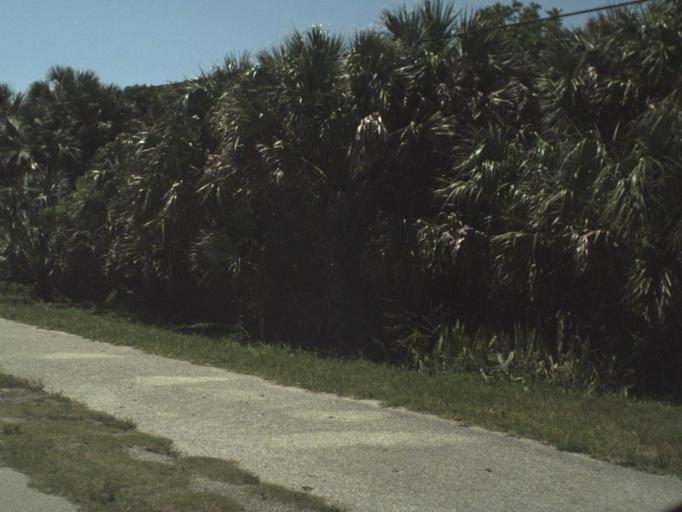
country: US
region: Florida
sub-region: Brevard County
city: Micco
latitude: 27.9084
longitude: -80.4753
